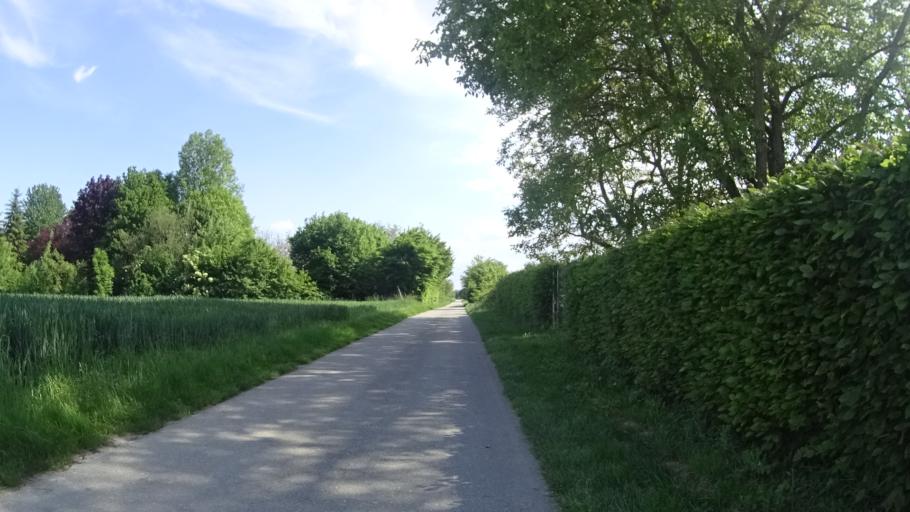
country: DE
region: Baden-Wuerttemberg
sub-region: Freiburg Region
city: Vogtsburg
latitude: 48.0891
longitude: 7.5939
